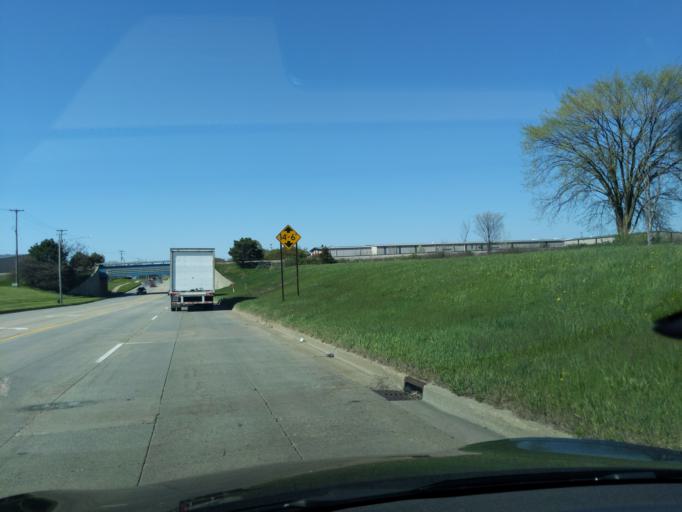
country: US
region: Michigan
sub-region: Kent County
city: East Grand Rapids
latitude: 42.8931
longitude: -85.5476
